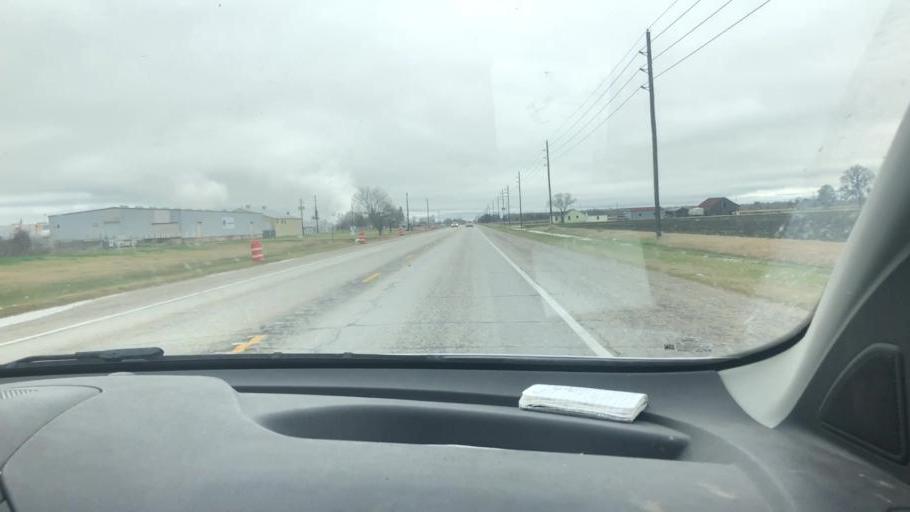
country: US
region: Texas
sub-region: Wharton County
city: Wharton
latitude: 29.2999
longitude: -96.0780
